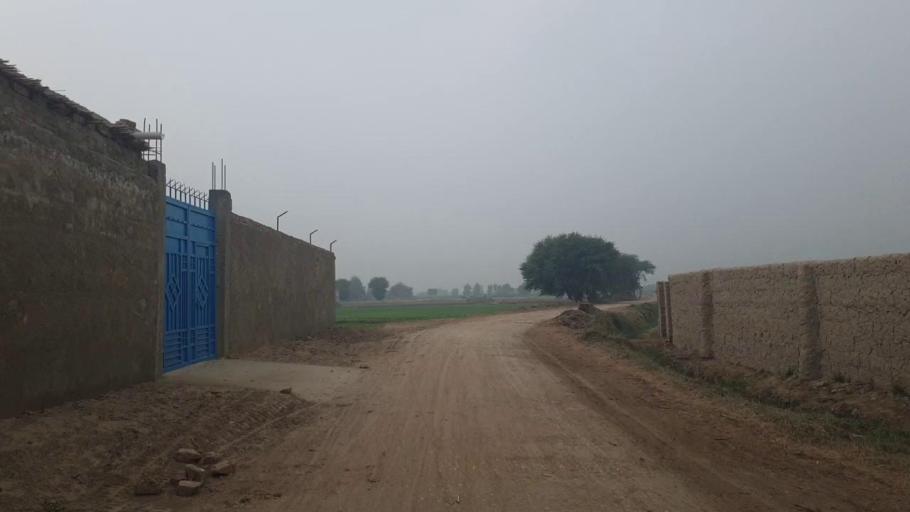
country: PK
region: Sindh
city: Tando Adam
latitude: 25.7124
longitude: 68.6174
